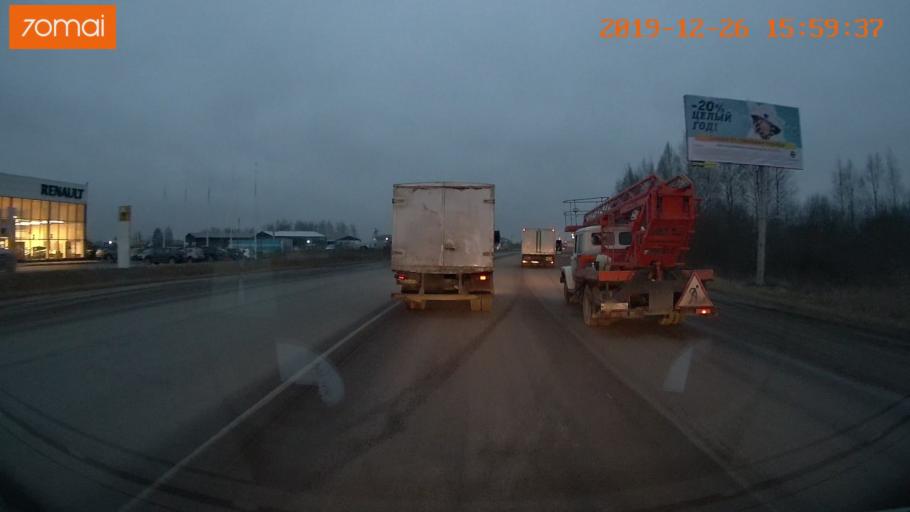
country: RU
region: Jaroslavl
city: Rybinsk
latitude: 58.0303
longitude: 38.8046
